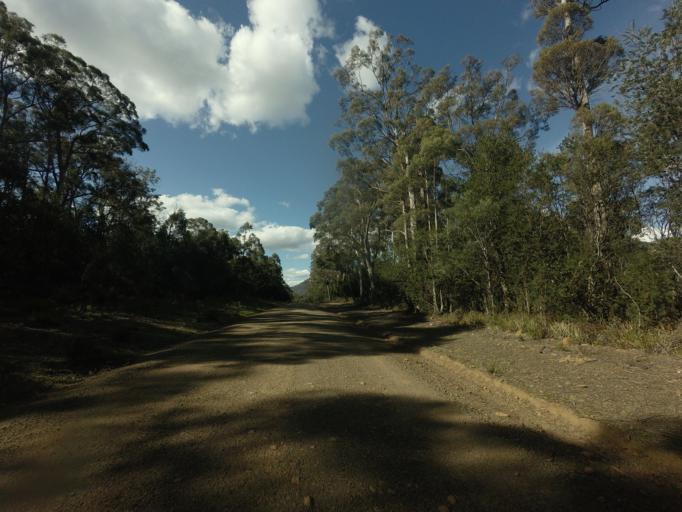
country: AU
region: Tasmania
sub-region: Break O'Day
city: St Helens
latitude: -41.8462
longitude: 148.0118
